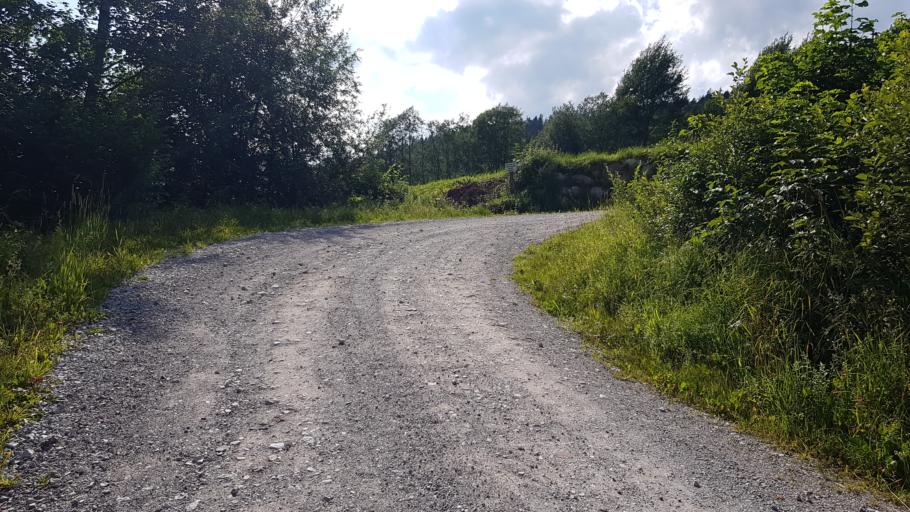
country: AT
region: Salzburg
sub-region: Politischer Bezirk Zell am See
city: Maria Alm am Steinernen Meer
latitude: 47.4183
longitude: 12.9295
